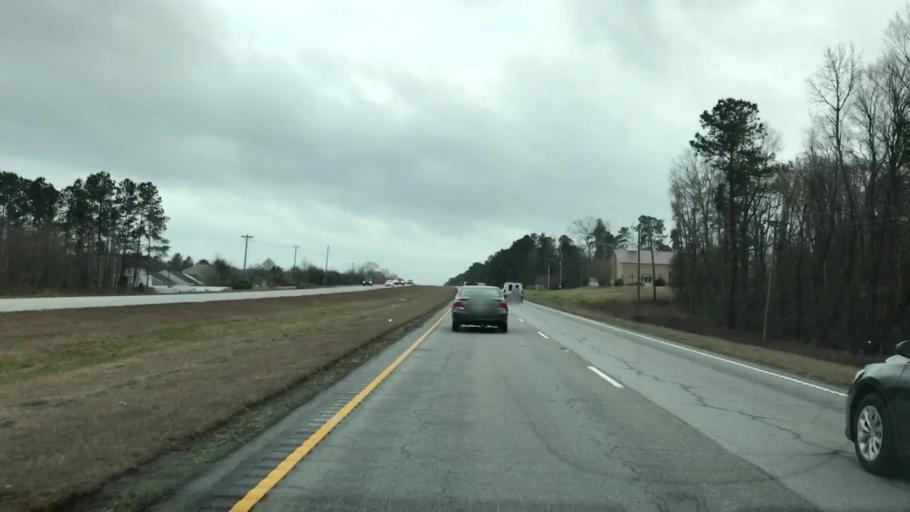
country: US
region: South Carolina
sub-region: Berkeley County
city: Moncks Corner
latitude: 33.1384
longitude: -80.0322
